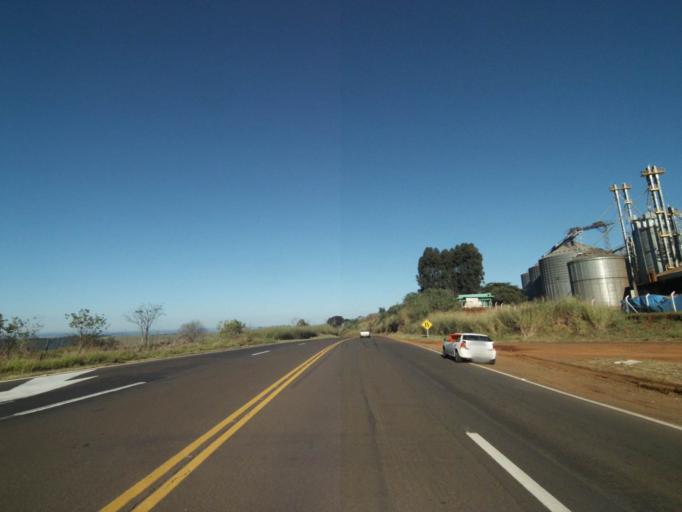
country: BR
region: Parana
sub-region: Londrina
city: Londrina
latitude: -23.5233
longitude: -51.1398
